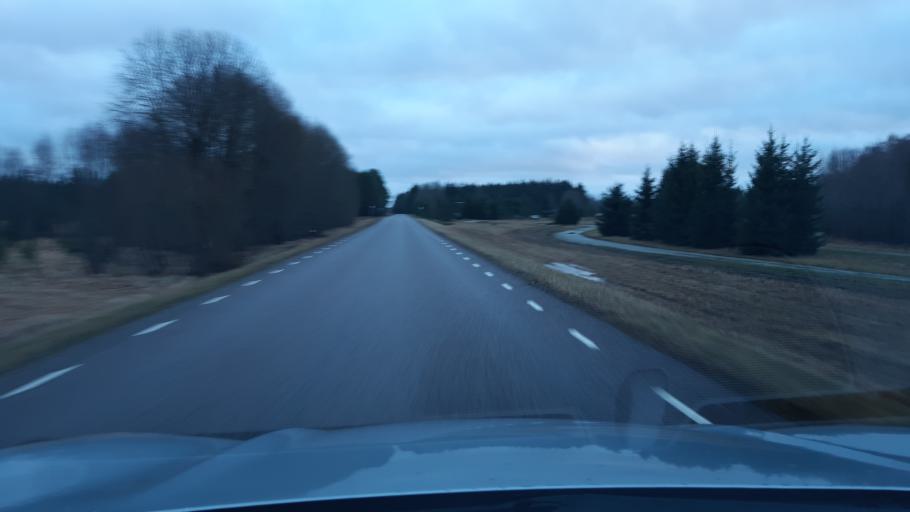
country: EE
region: Raplamaa
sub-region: Kohila vald
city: Kohila
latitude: 59.1292
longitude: 24.6676
